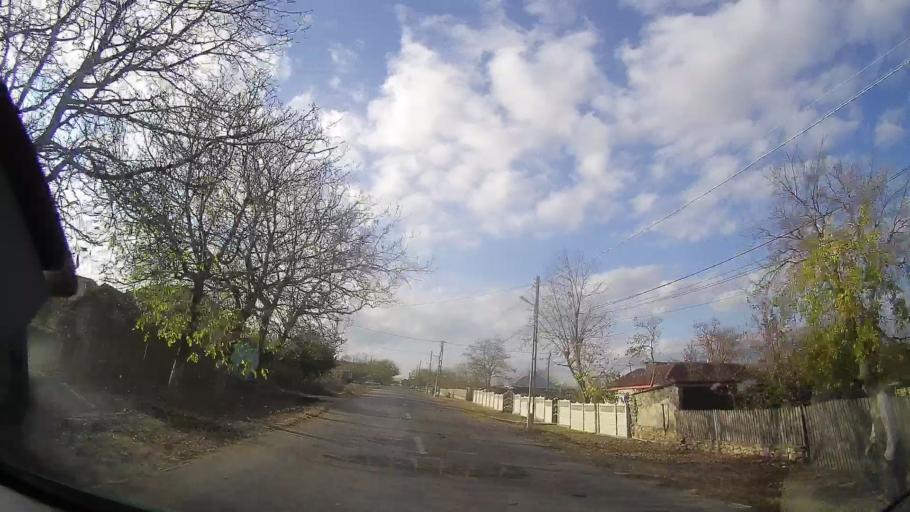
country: RO
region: Constanta
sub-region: Comuna Comana
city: Comana
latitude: 43.8230
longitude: 28.3372
